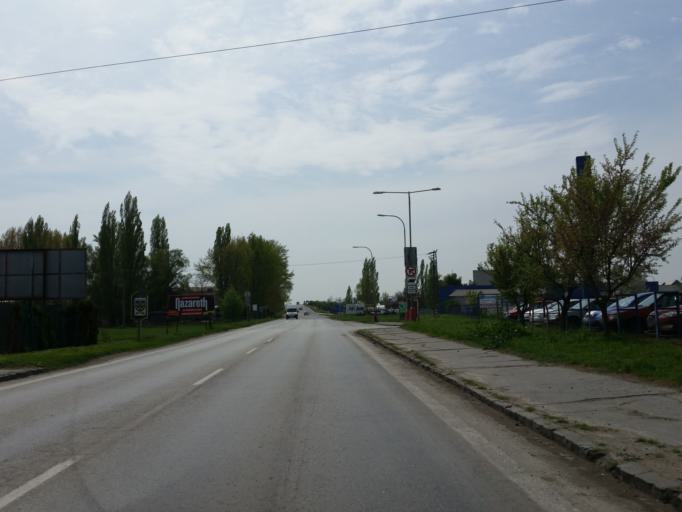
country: SK
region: Trnavsky
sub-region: Okres Galanta
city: Galanta
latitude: 48.2636
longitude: 17.7476
